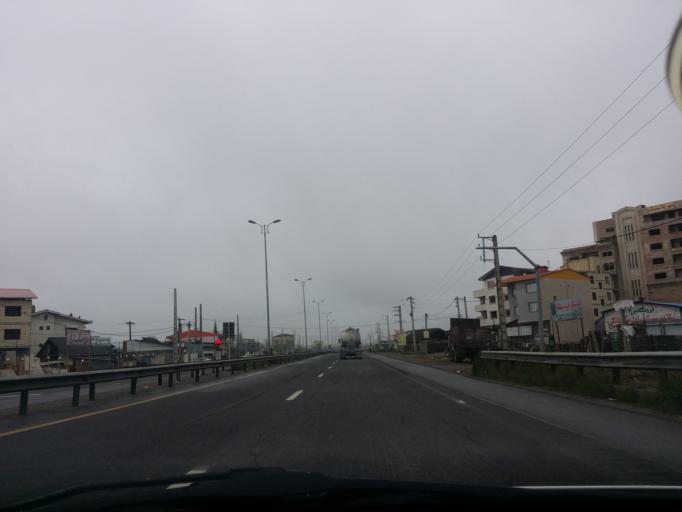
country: IR
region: Mazandaran
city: Tonekabon
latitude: 36.7959
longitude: 50.9109
